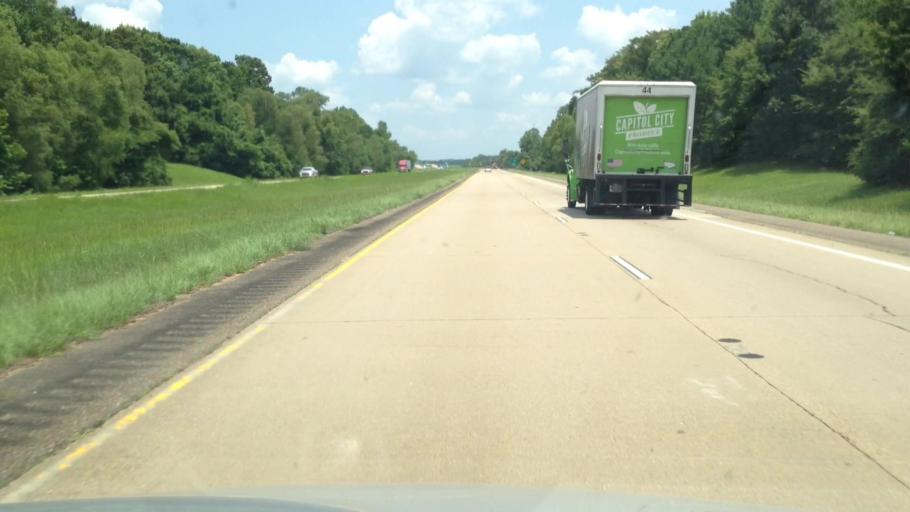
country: US
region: Louisiana
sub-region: Rapides Parish
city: Lecompte
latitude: 31.0222
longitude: -92.3936
